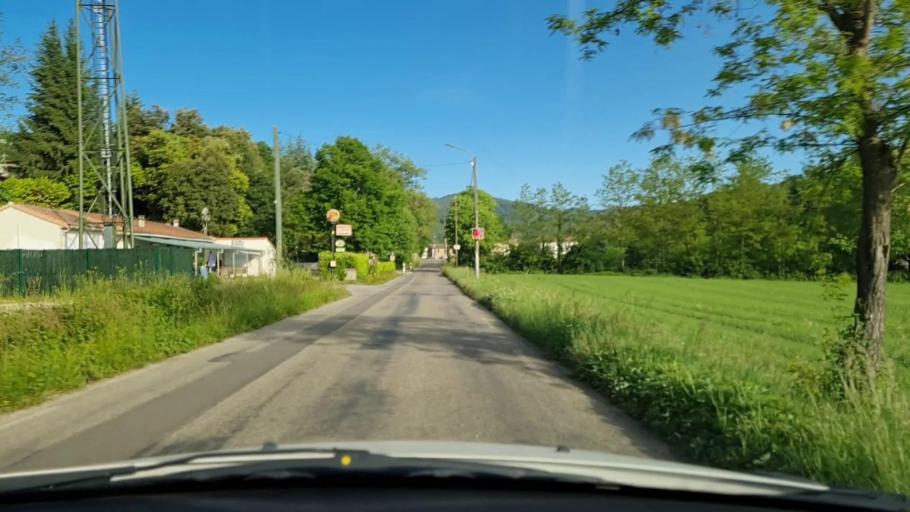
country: FR
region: Languedoc-Roussillon
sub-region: Departement du Gard
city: Cendras
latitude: 44.1531
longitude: 4.0408
